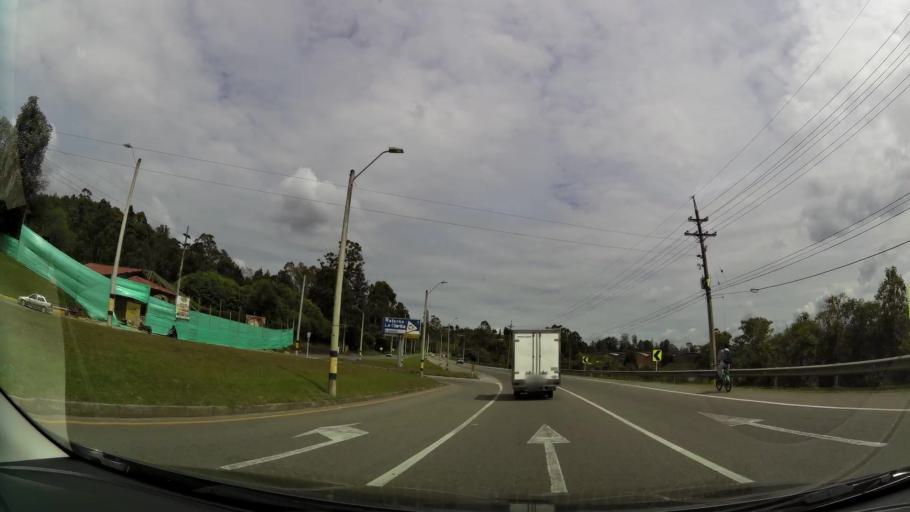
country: CO
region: Antioquia
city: Guarne
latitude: 6.2440
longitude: -75.4212
